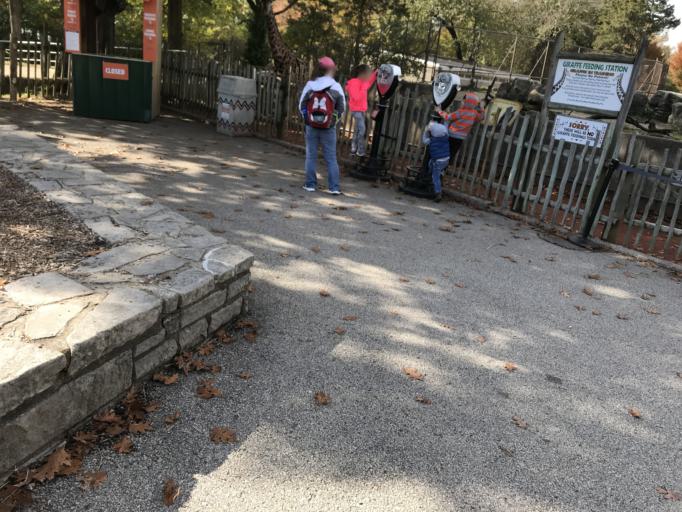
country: US
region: Kentucky
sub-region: Jefferson County
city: Audubon Park
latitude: 38.2059
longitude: -85.7041
